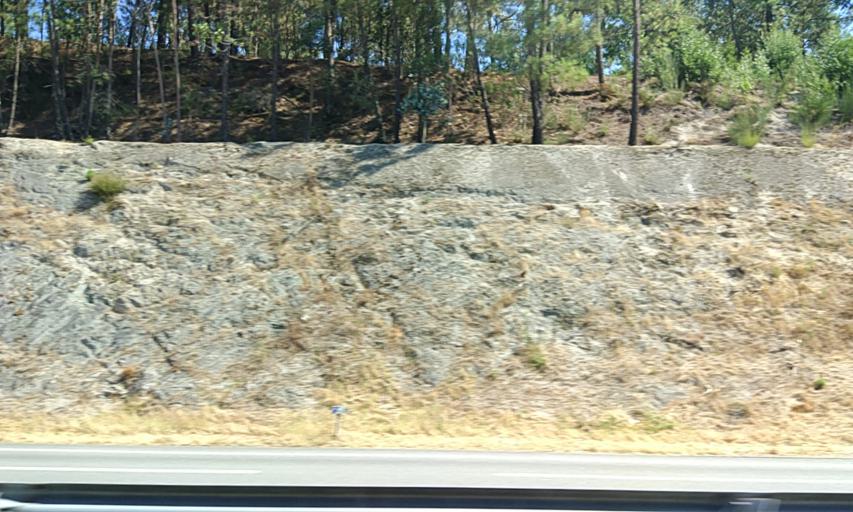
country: PT
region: Porto
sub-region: Marco de Canaveses
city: Marco de Canavezes
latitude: 41.2302
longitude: -8.1911
